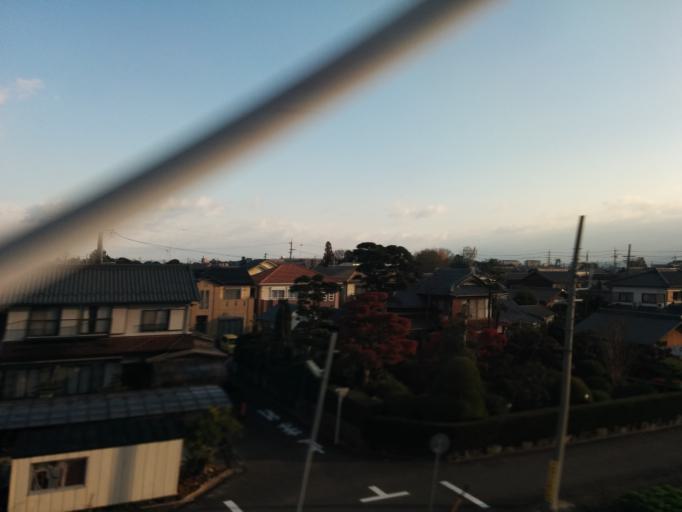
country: JP
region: Aichi
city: Inazawa
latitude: 35.2382
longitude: 136.7832
